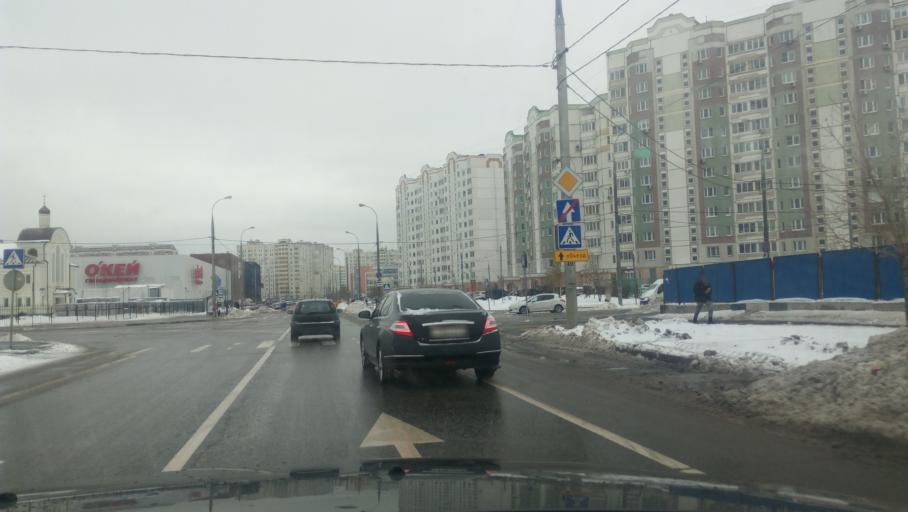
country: RU
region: Moscow
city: Zhulebino
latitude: 55.7136
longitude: 37.8787
